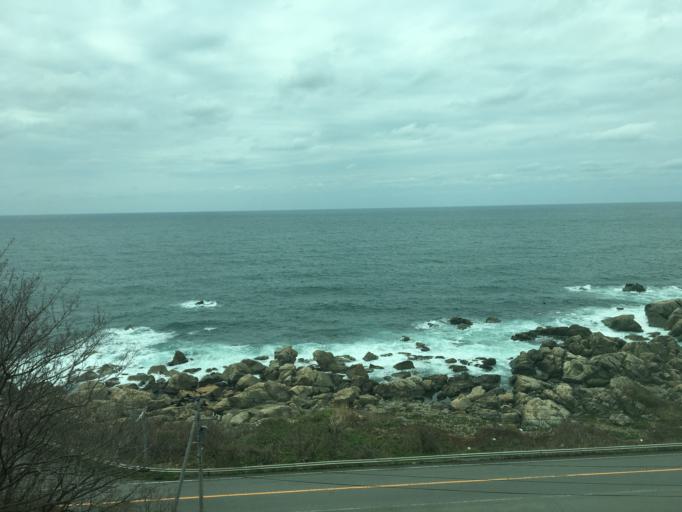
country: JP
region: Akita
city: Noshiromachi
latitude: 40.4425
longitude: 139.9411
